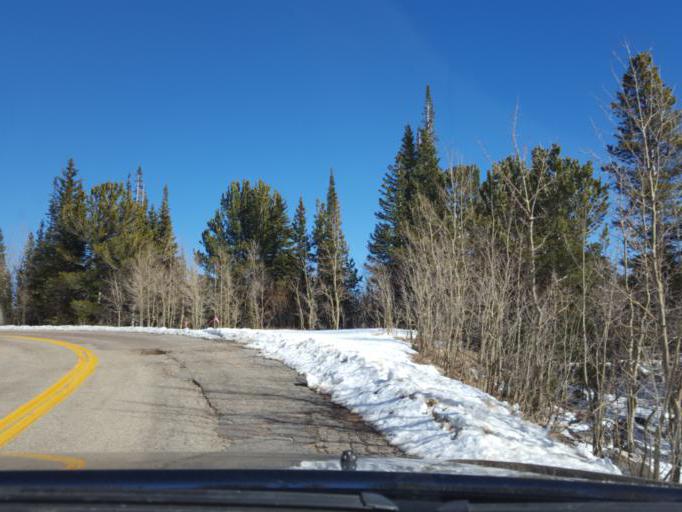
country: US
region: Colorado
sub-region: Boulder County
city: Nederland
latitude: 40.0787
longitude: -105.5248
